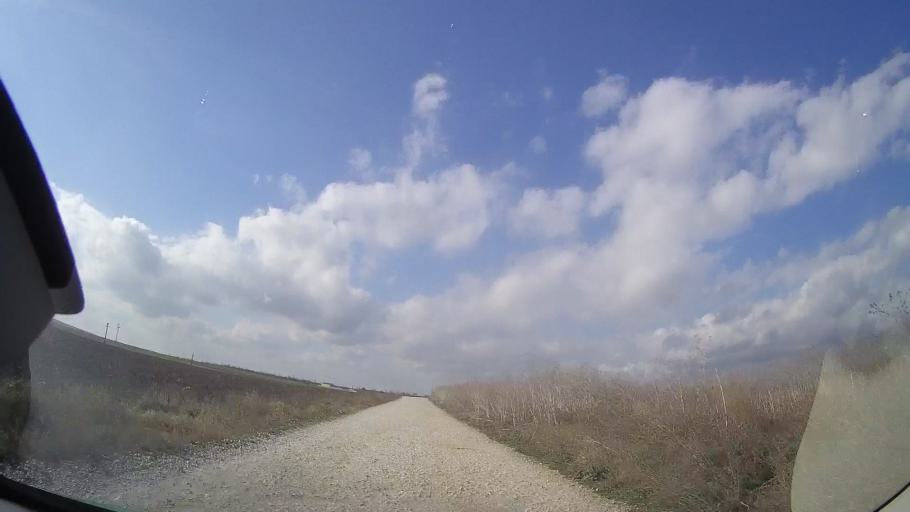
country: RO
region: Constanta
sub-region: Comuna Douazeci si Trei August
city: Douazeci si Trei August
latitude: 43.9118
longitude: 28.5919
